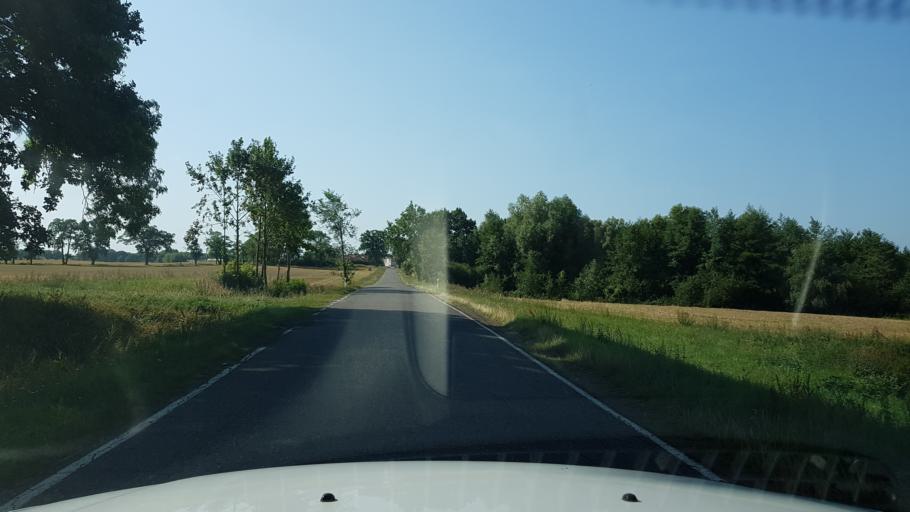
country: PL
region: West Pomeranian Voivodeship
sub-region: Powiat stargardzki
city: Dolice
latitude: 53.1234
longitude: 15.2548
